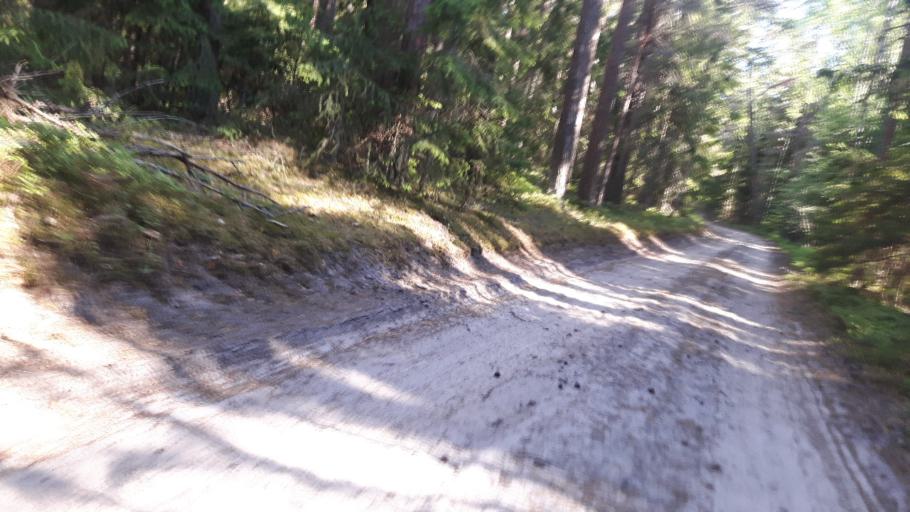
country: LV
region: Salacgrivas
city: Salacgriva
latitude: 57.7196
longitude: 24.3477
